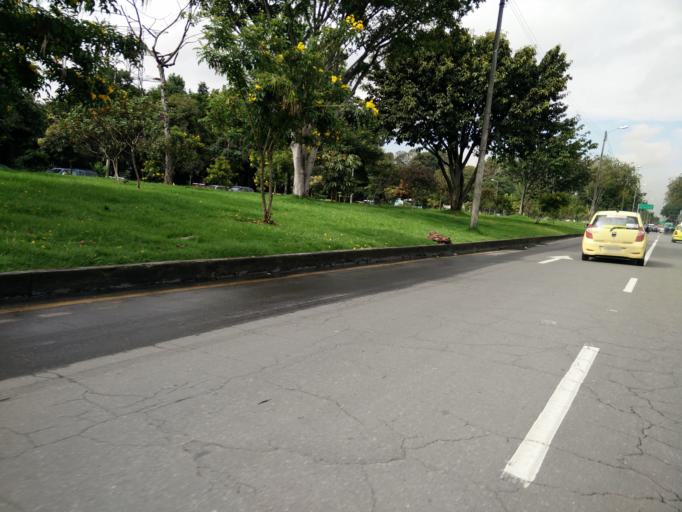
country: CO
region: Bogota D.C.
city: Bogota
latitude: 4.6702
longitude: -74.1020
